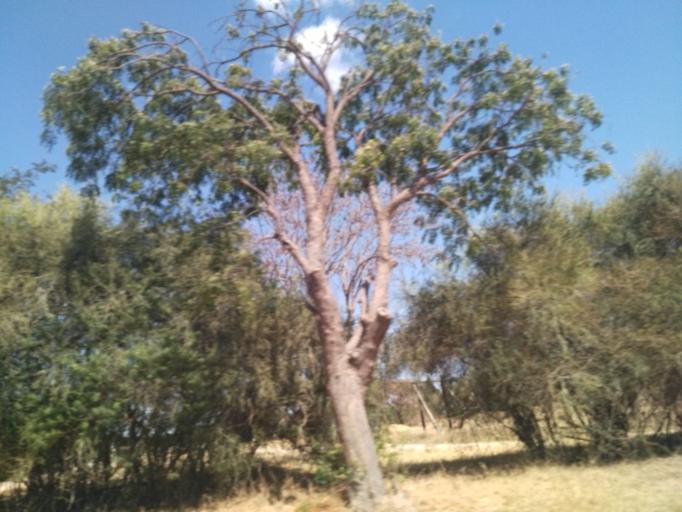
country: TZ
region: Dodoma
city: Dodoma
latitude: -6.1623
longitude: 35.7525
